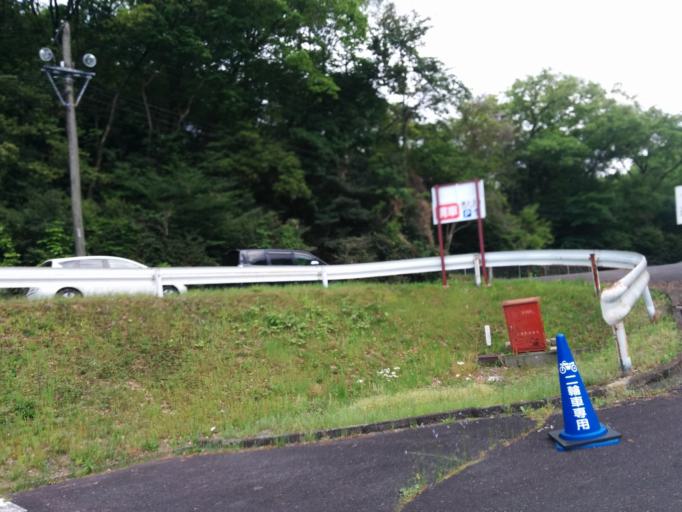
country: JP
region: Gifu
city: Inuyama
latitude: 35.3485
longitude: 136.9868
